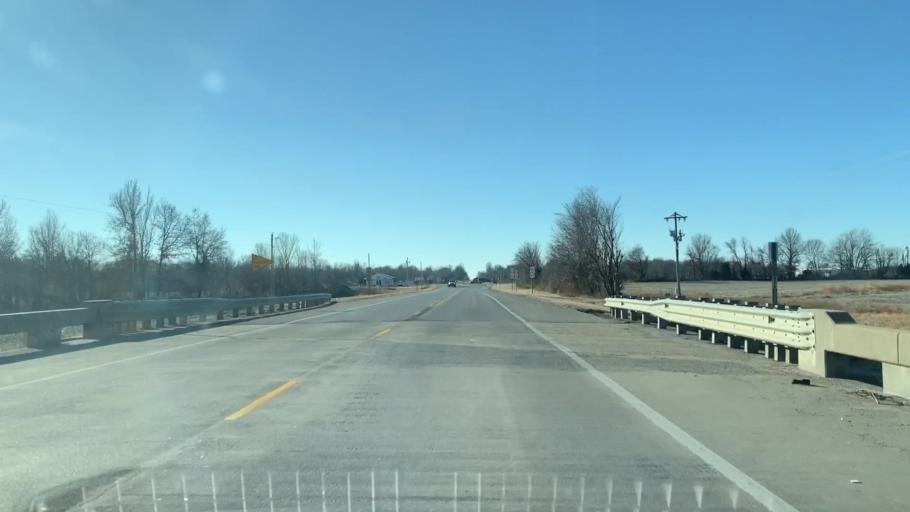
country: US
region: Kansas
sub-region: Cherokee County
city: Galena
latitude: 37.1825
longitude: -94.7046
